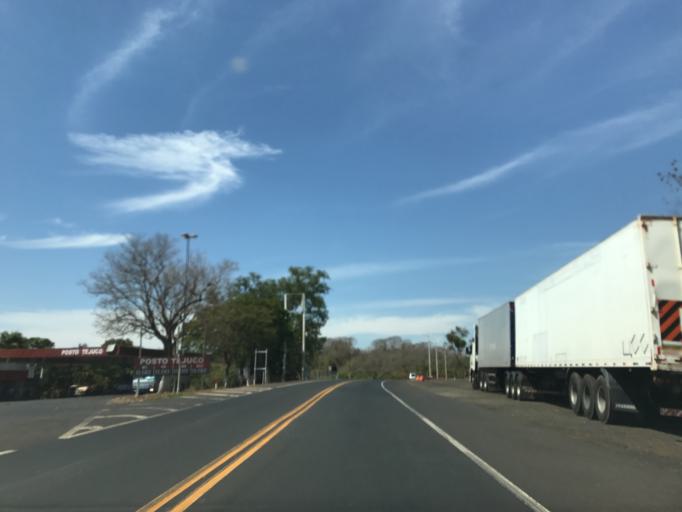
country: BR
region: Minas Gerais
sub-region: Monte Alegre De Minas
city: Monte Alegre de Minas
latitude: -19.0411
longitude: -49.0103
